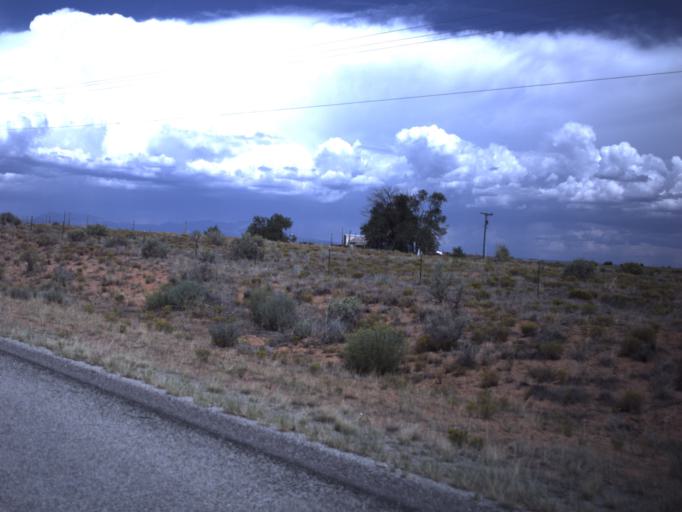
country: US
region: Utah
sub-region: San Juan County
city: Blanding
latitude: 37.4797
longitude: -109.4690
